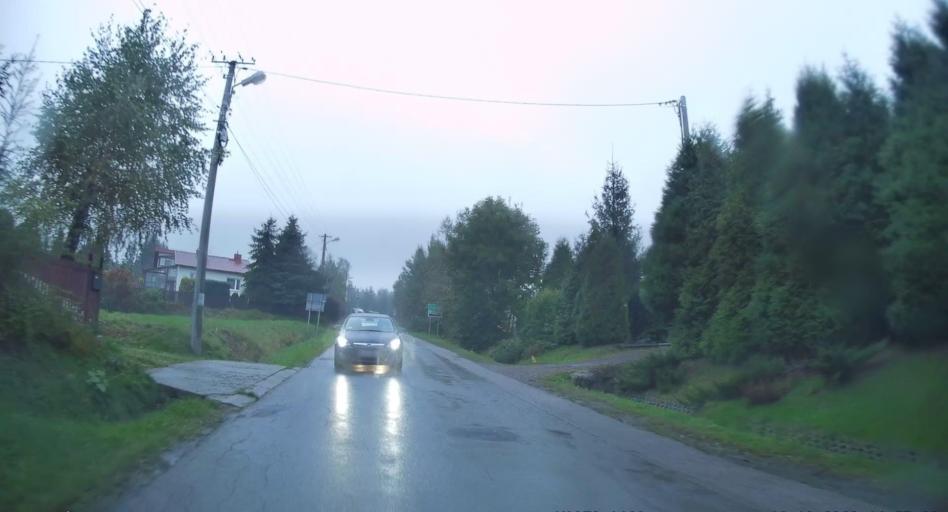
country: PL
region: Lesser Poland Voivodeship
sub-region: Powiat krakowski
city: Ochojno
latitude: 49.9727
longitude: 19.9997
